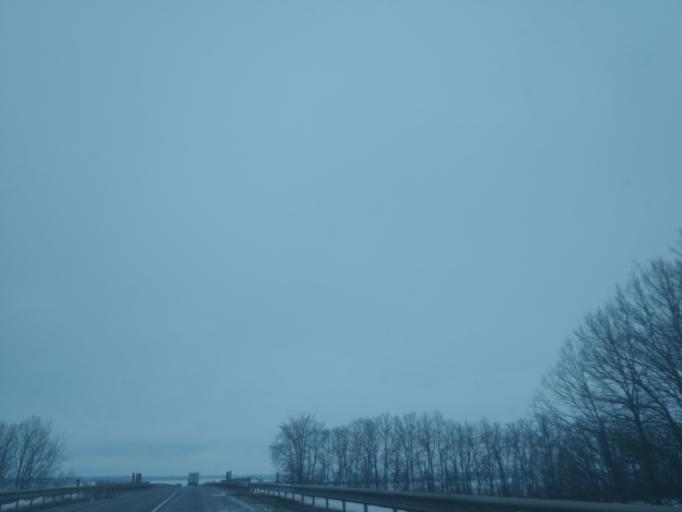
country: BY
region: Minsk
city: Haradzyeya
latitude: 53.3291
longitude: 26.5494
